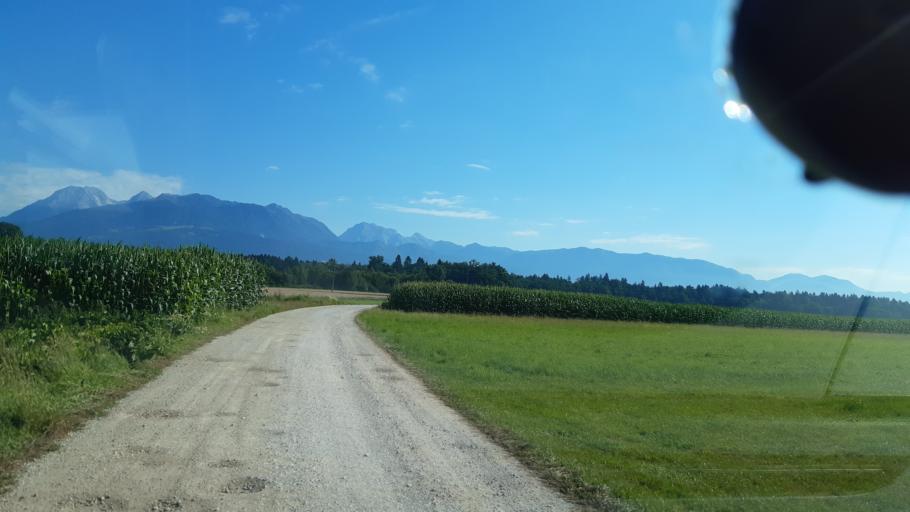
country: SI
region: Vodice
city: Vodice
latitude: 46.1897
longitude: 14.5085
